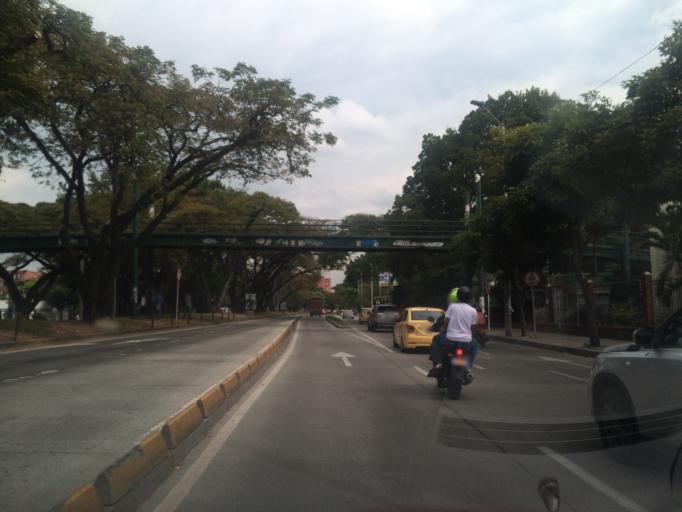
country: CO
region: Valle del Cauca
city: Cali
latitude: 3.4036
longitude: -76.5469
